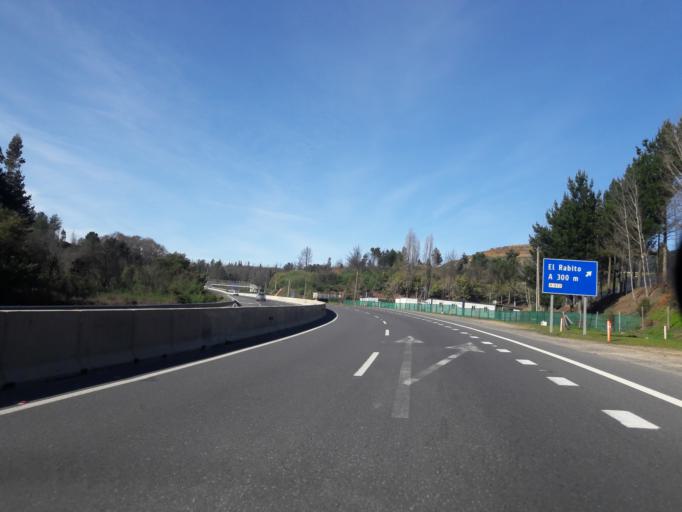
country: CL
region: Biobio
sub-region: Provincia de Concepcion
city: Chiguayante
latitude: -36.8628
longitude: -72.8576
